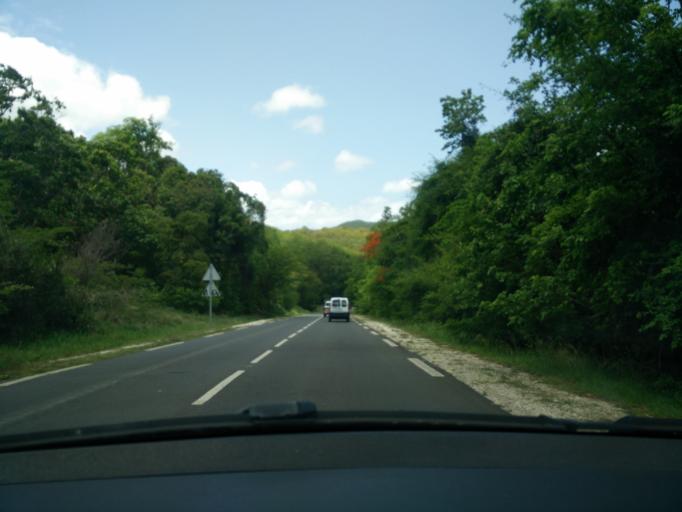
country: GP
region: Guadeloupe
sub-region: Guadeloupe
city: Sainte-Rose
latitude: 16.3509
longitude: -61.7660
